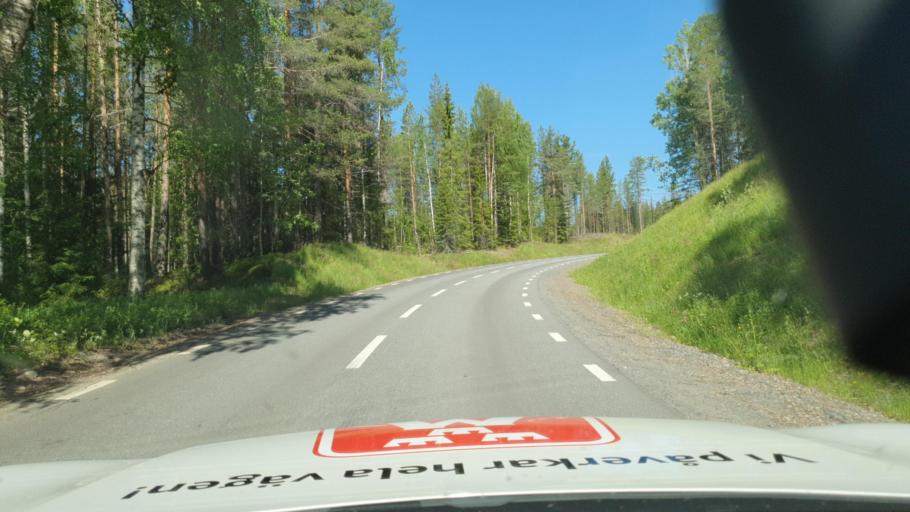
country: SE
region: Vaesterbotten
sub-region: Skelleftea Kommun
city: Boliden
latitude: 64.7953
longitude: 20.3341
